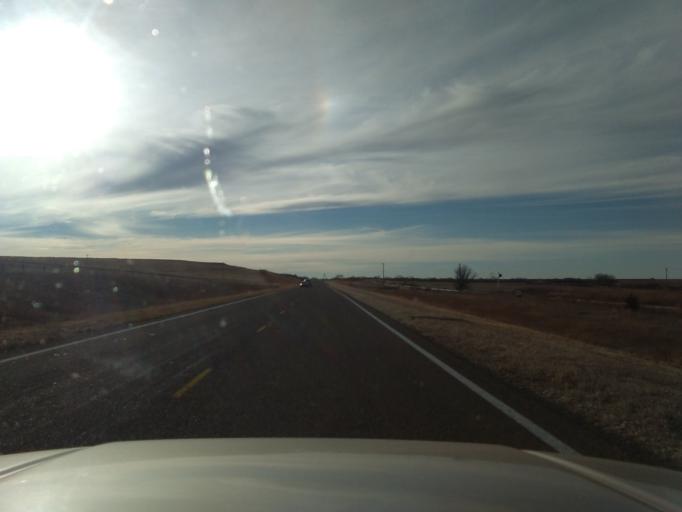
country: US
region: Kansas
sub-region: Norton County
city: Norton
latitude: 39.7489
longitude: -100.1491
